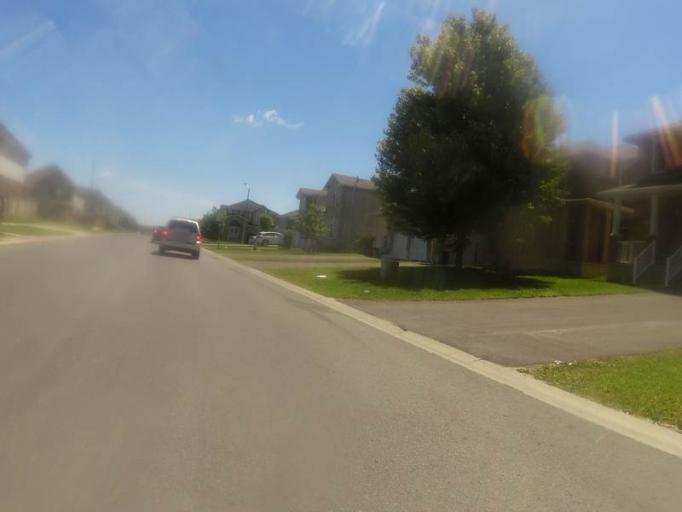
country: CA
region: Ontario
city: Kingston
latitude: 44.2643
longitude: -76.5581
